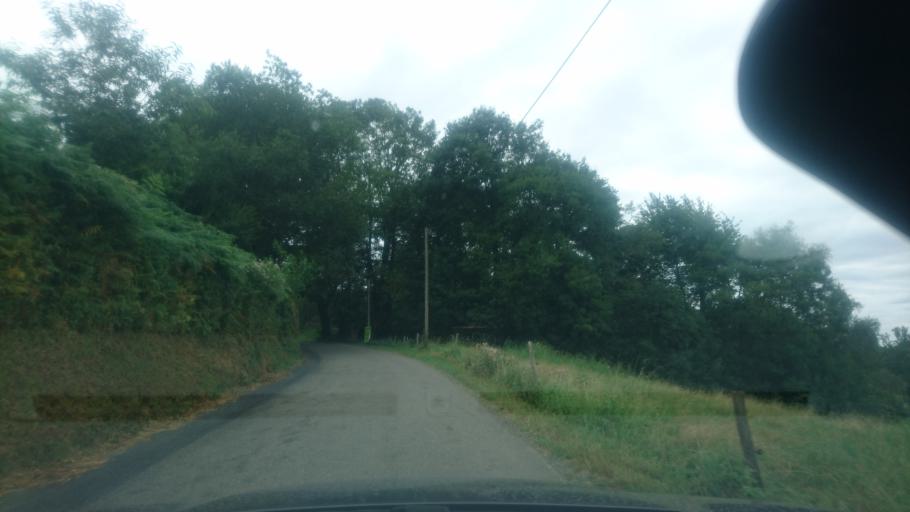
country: FR
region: Midi-Pyrenees
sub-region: Departement des Hautes-Pyrenees
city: Odos
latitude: 43.1345
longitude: 0.0529
